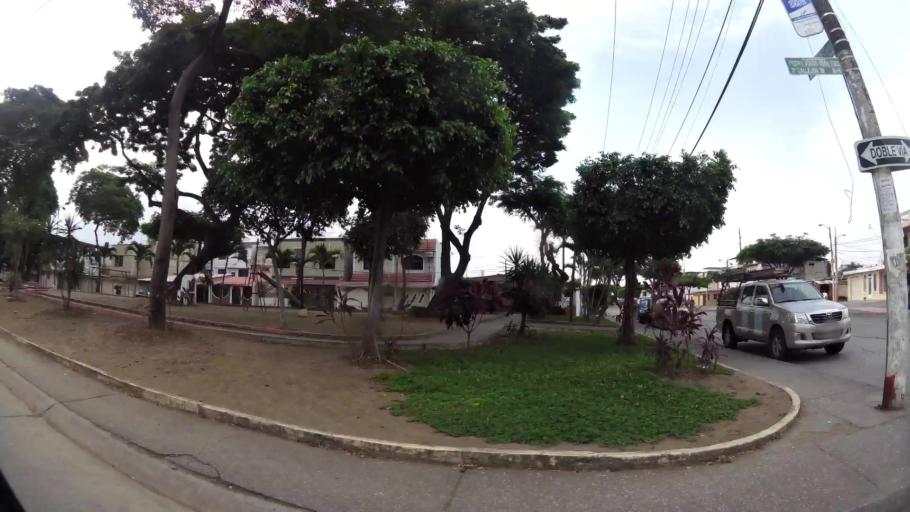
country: EC
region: Guayas
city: Eloy Alfaro
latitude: -2.1195
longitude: -79.8896
